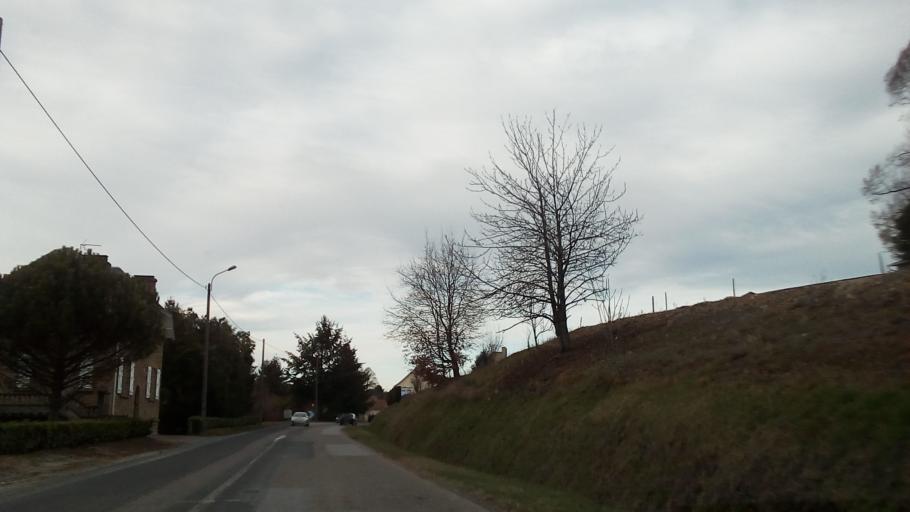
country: FR
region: Limousin
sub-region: Departement de la Correze
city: Naves
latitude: 45.3132
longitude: 1.7715
